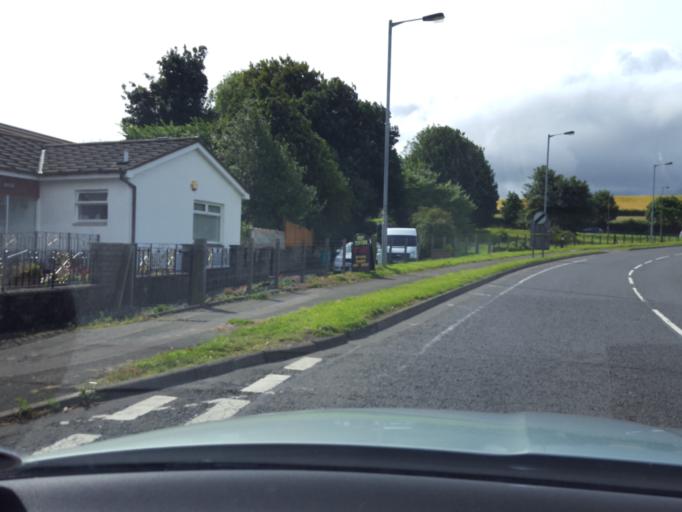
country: GB
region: Scotland
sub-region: West Lothian
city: Linlithgow
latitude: 56.0067
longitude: -3.5748
